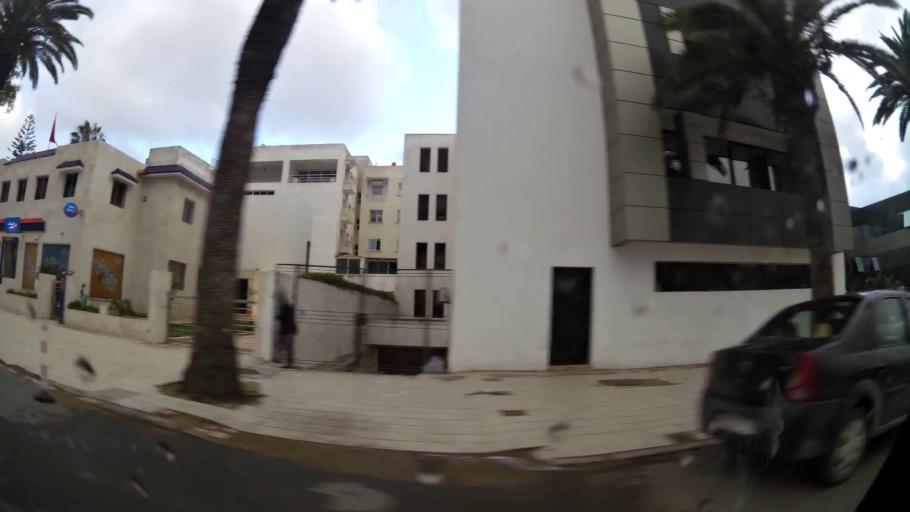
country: MA
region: Doukkala-Abda
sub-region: El-Jadida
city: El Jadida
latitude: 33.2506
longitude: -8.4996
